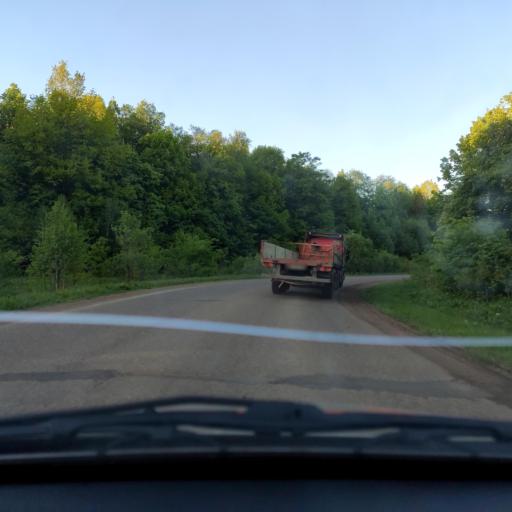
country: RU
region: Bashkortostan
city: Blagoveshchensk
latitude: 55.0345
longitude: 56.1164
